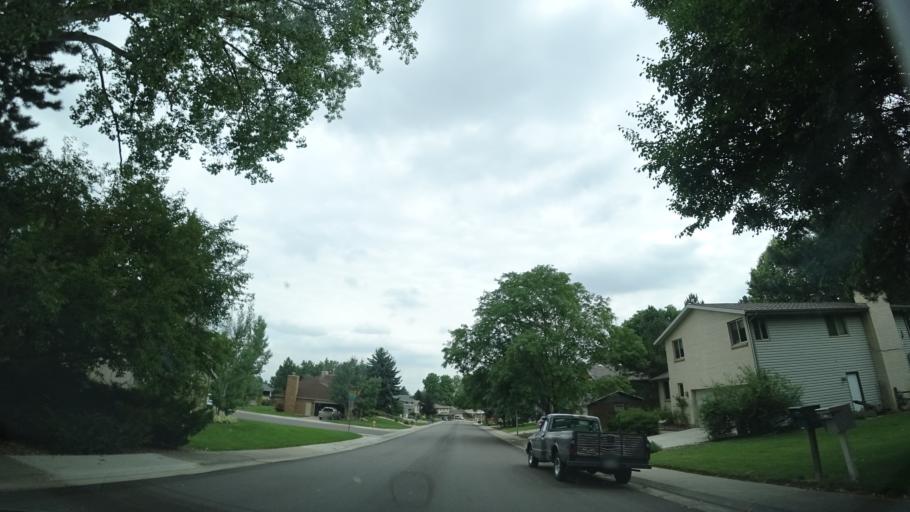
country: US
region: Colorado
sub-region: Jefferson County
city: West Pleasant View
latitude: 39.7221
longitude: -105.1576
